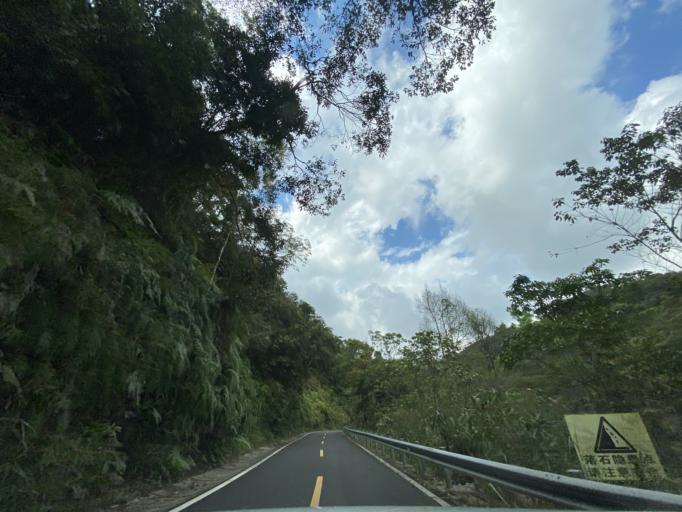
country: CN
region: Hainan
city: Benhao
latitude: 18.6978
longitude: 109.8788
